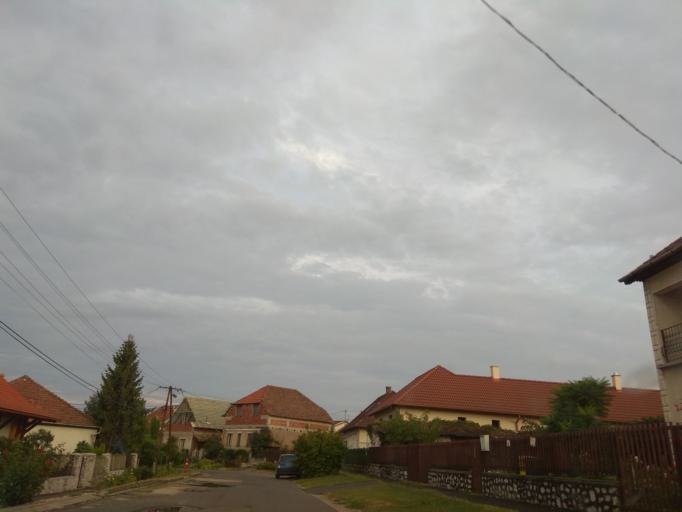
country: HU
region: Borsod-Abauj-Zemplen
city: Miskolc
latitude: 48.0524
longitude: 20.7889
